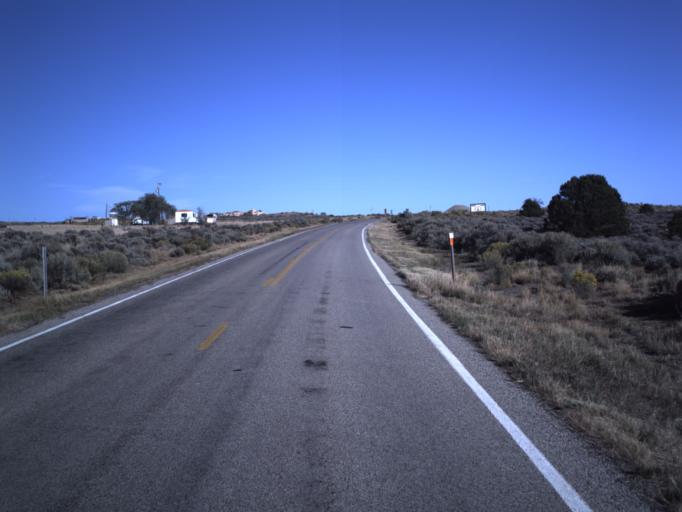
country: US
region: Utah
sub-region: Grand County
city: Moab
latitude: 38.3163
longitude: -109.3116
